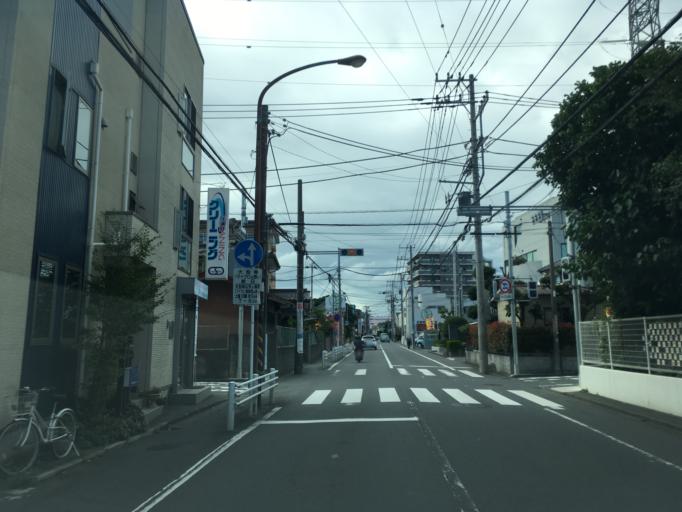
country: JP
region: Tokyo
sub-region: Machida-shi
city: Machida
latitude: 35.5581
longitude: 139.4114
